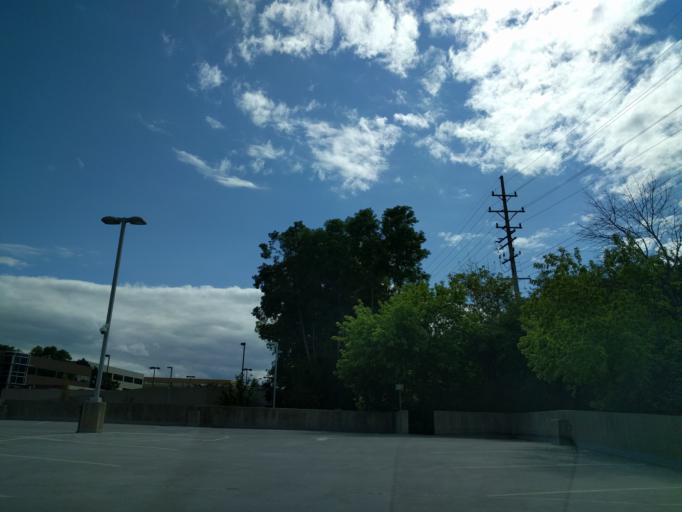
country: US
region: Wisconsin
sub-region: Waukesha County
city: Elm Grove
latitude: 43.0448
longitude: -88.0491
